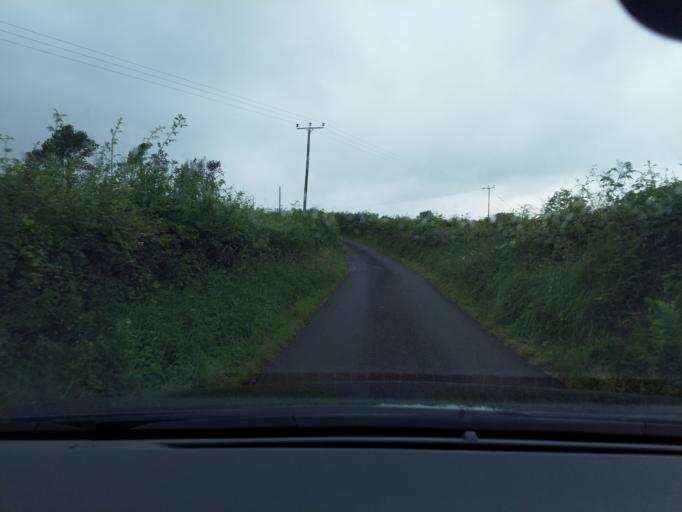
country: GB
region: Northern Ireland
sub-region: Dungannon District
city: Dungannon
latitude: 54.4032
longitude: -6.7768
